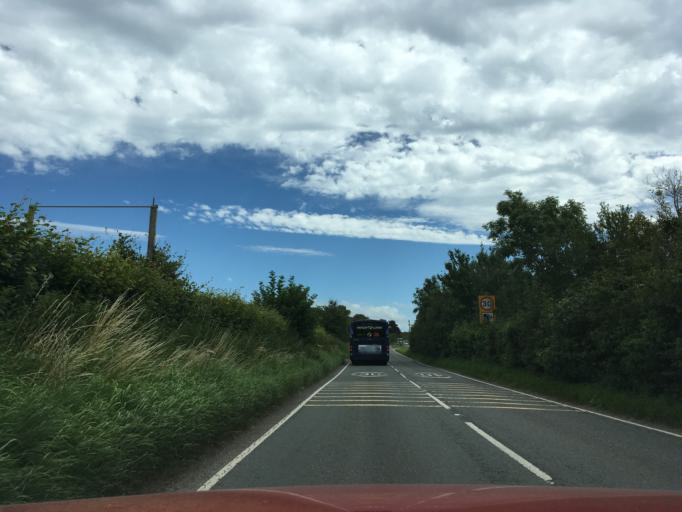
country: GB
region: England
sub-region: Somerset
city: Bradley Cross
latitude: 51.2603
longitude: -2.7565
